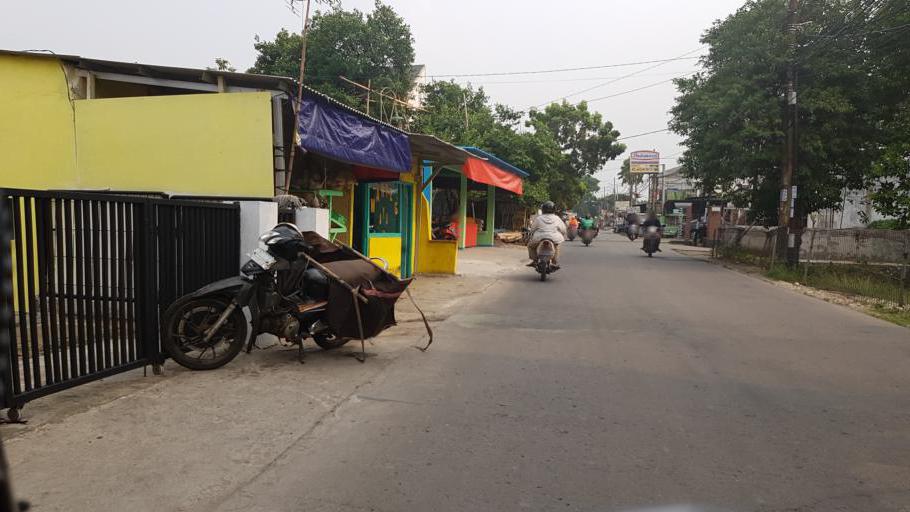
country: ID
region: West Java
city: Depok
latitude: -6.3691
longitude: 106.8427
